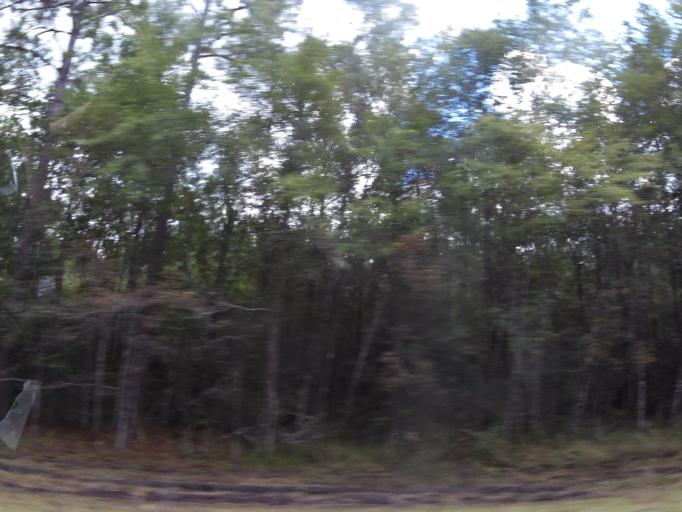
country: US
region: Georgia
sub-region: Charlton County
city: Folkston
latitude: 31.0029
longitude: -82.0268
